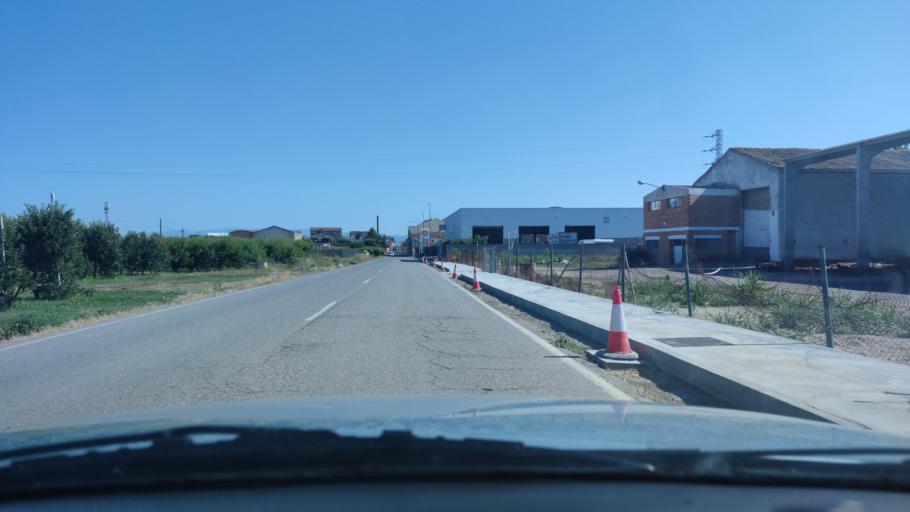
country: ES
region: Catalonia
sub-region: Provincia de Lleida
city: Bellvis
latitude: 41.6688
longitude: 0.8139
